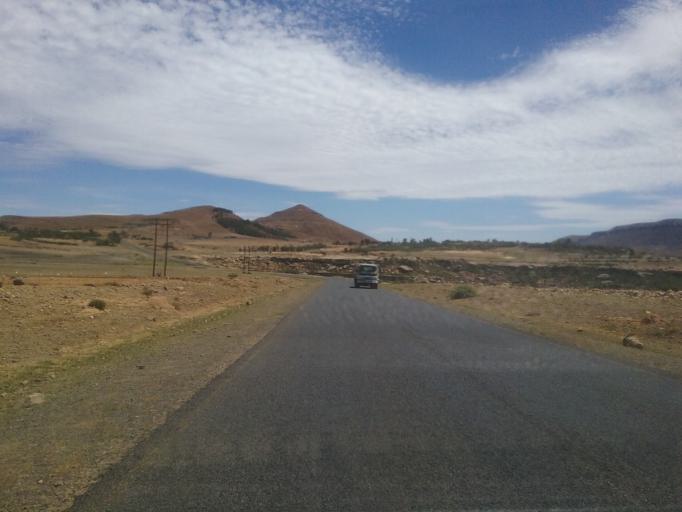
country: LS
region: Mafeteng
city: Mafeteng
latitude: -29.9264
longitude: 27.2569
